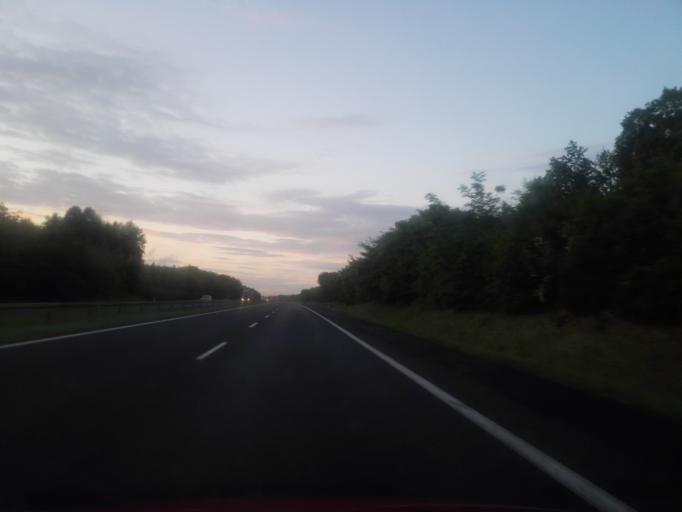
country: PL
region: Lodz Voivodeship
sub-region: Powiat radomszczanski
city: Radomsko
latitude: 51.0703
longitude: 19.3677
